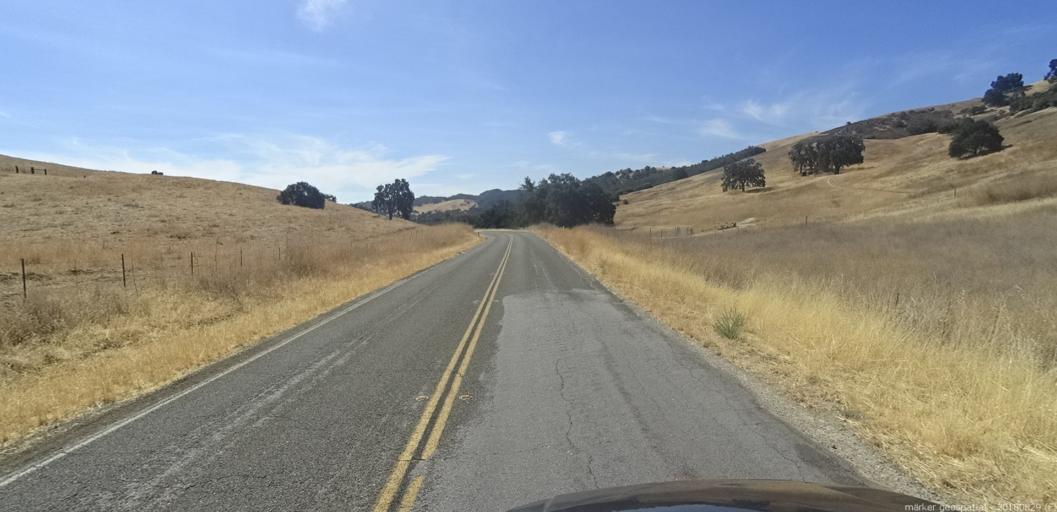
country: US
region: California
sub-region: San Luis Obispo County
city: Lake Nacimiento
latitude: 35.8478
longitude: -121.0495
